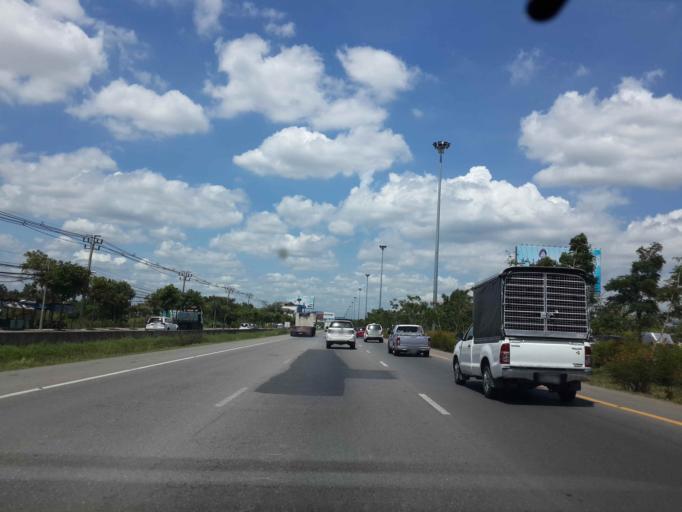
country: TH
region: Bangkok
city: Bang Bon
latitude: 13.6296
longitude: 100.3967
